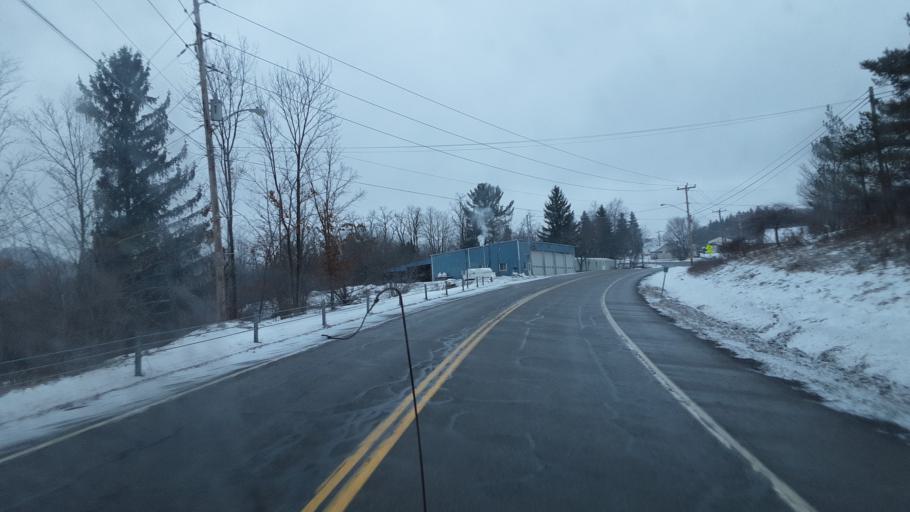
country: US
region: Pennsylvania
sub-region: Tioga County
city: Westfield
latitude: 42.0390
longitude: -77.5441
